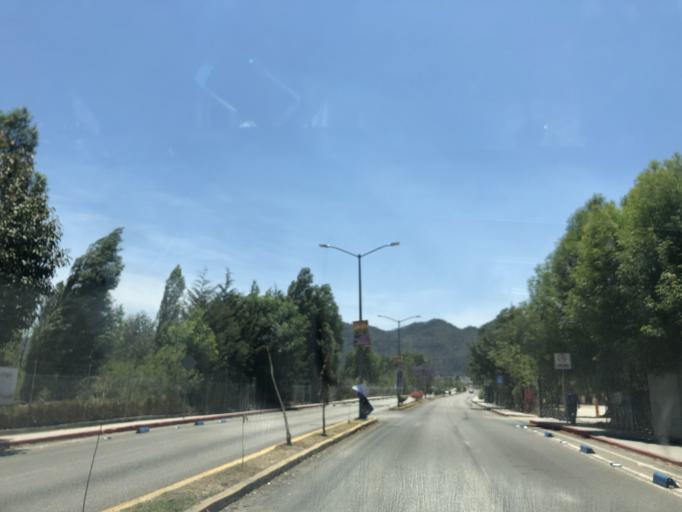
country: MX
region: Chiapas
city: San Cristobal de las Casas
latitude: 16.7303
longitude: -92.6511
